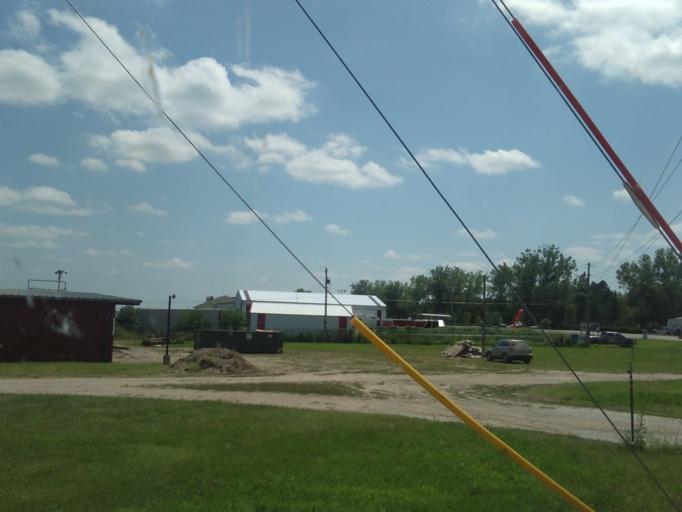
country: US
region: Nebraska
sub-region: Gosper County
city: Elwood
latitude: 40.6846
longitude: -99.8277
